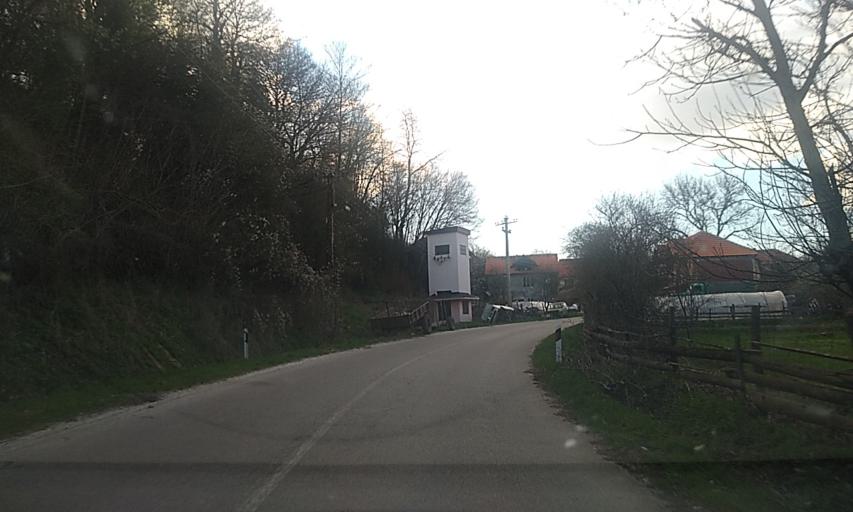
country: RS
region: Central Serbia
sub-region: Pcinjski Okrug
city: Bosilegrad
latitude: 42.4666
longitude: 22.4845
